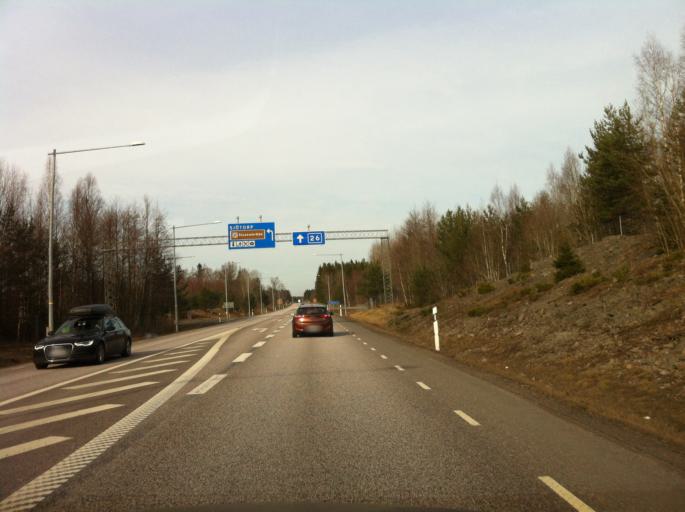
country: SE
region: Vaestra Goetaland
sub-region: Toreboda Kommun
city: Toereboda
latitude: 58.8290
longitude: 13.9891
